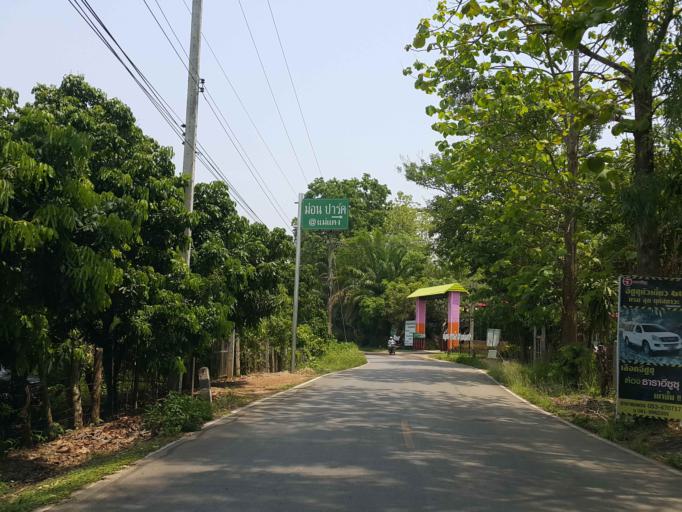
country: TH
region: Chiang Mai
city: Mae Taeng
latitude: 19.0931
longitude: 98.9019
